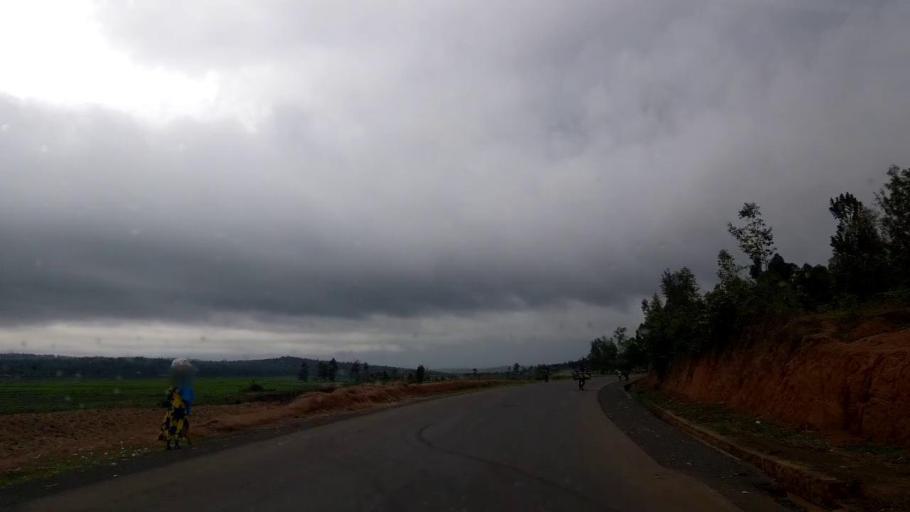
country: RW
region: Northern Province
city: Byumba
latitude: -1.4447
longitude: 30.2505
